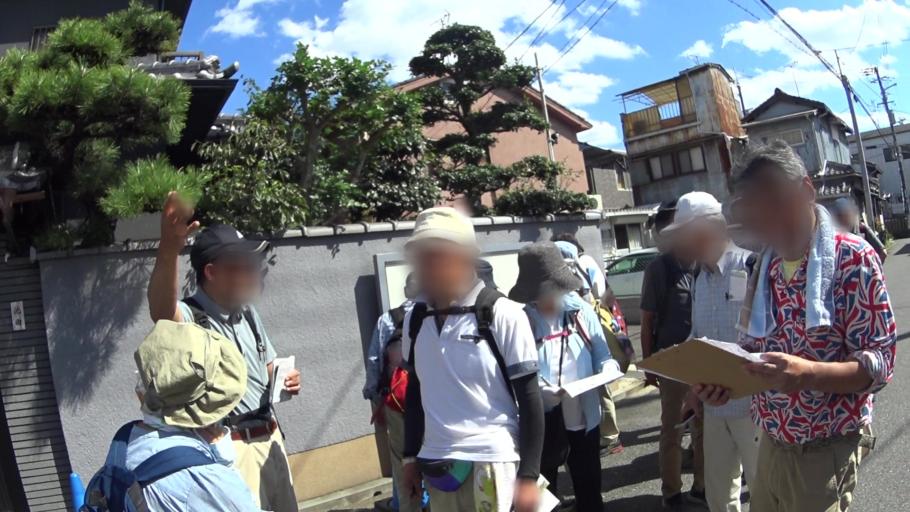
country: JP
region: Osaka
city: Yao
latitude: 34.6421
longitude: 135.5467
